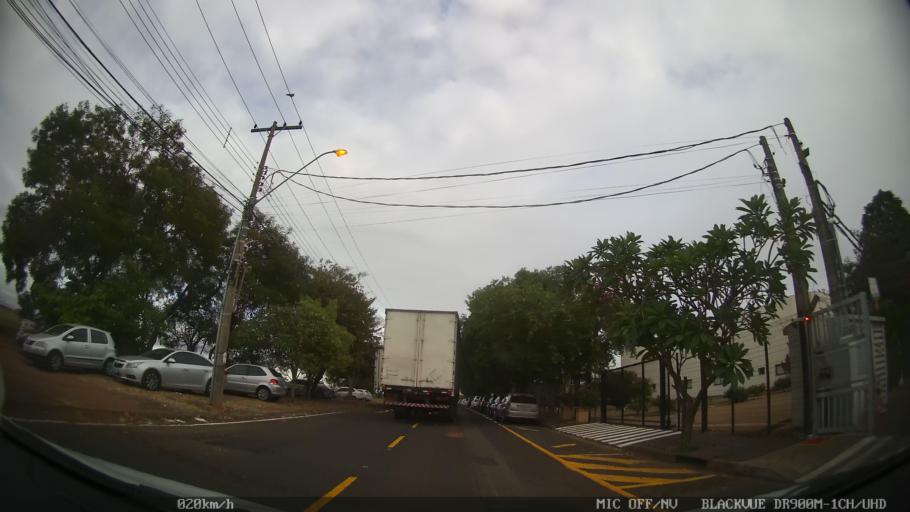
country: BR
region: Sao Paulo
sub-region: Sao Jose Do Rio Preto
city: Sao Jose do Rio Preto
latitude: -20.8295
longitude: -49.4219
